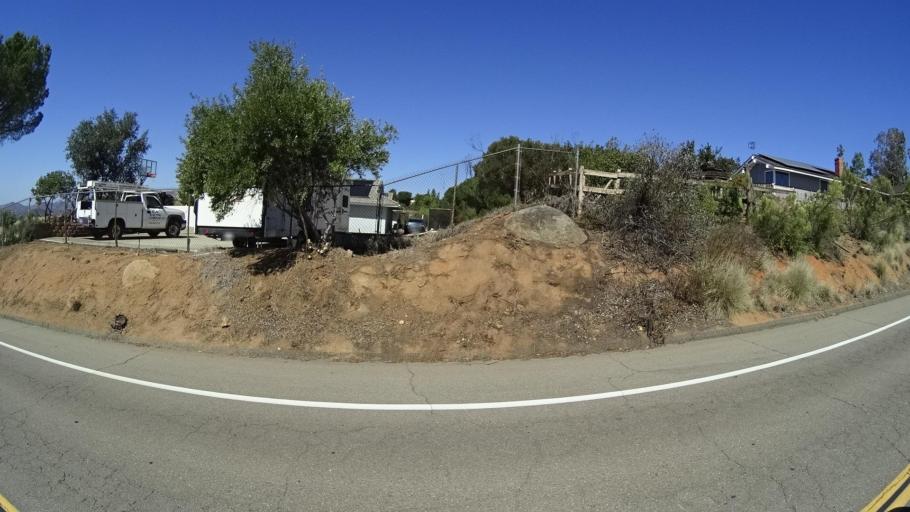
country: US
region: California
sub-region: San Diego County
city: Alpine
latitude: 32.8428
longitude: -116.7698
